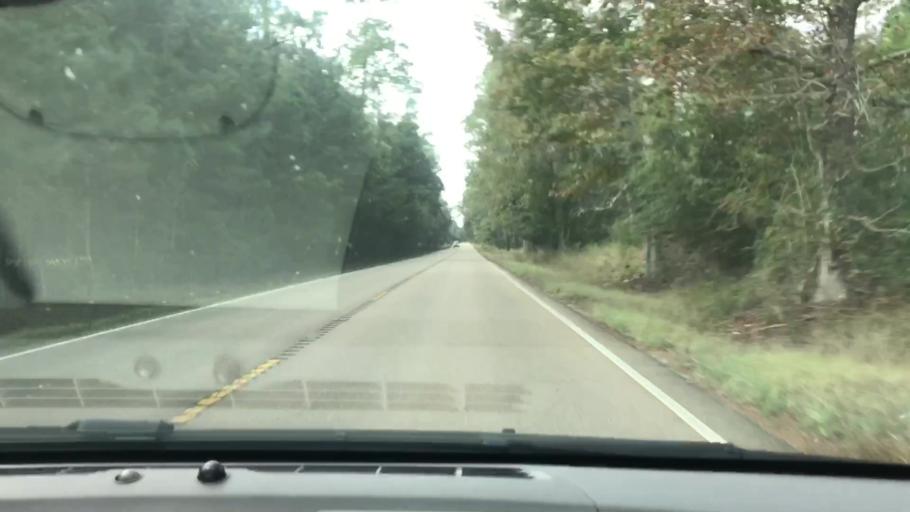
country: US
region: Louisiana
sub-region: Saint Tammany Parish
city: Abita Springs
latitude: 30.4988
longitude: -89.9990
